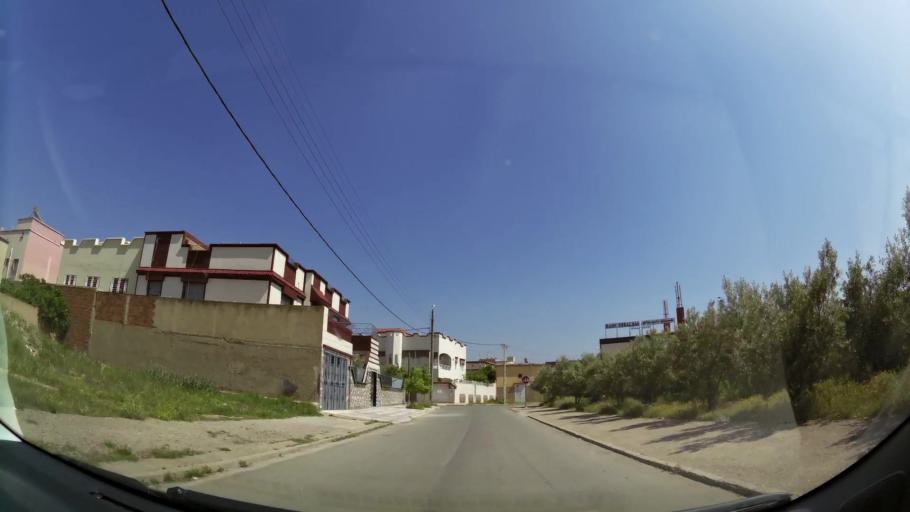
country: MA
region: Oriental
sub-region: Oujda-Angad
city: Oujda
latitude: 34.6865
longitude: -1.8781
